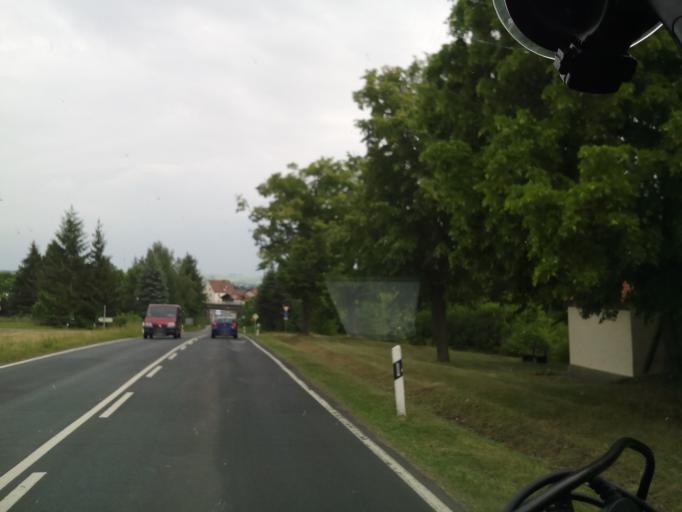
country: DE
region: Bavaria
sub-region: Regierungsbezirk Unterfranken
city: Stockheim
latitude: 50.4616
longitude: 10.2641
